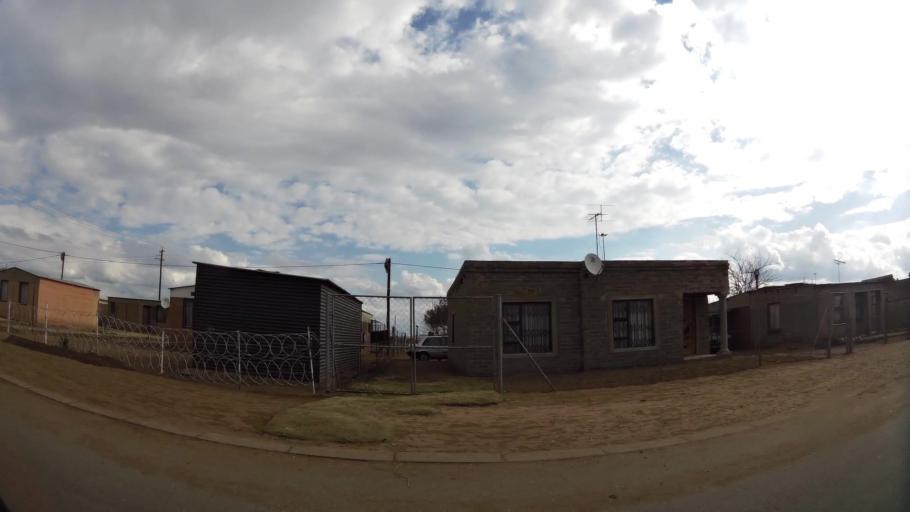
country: ZA
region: Gauteng
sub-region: Sedibeng District Municipality
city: Vanderbijlpark
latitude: -26.6856
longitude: 27.7796
